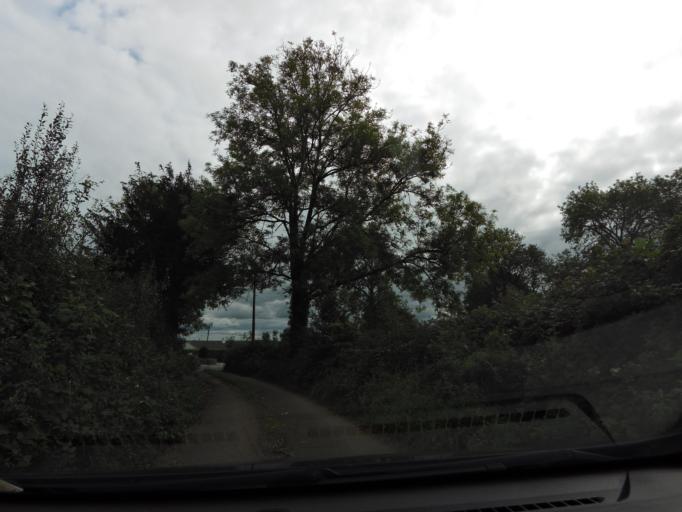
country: IE
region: Connaught
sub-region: County Galway
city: Loughrea
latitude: 53.1644
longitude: -8.4402
